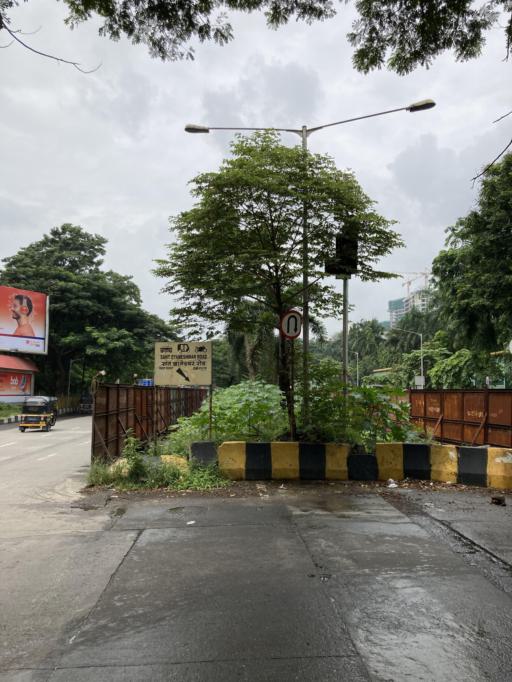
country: IN
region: Maharashtra
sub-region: Mumbai Suburban
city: Mumbai
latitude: 19.0582
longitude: 72.8537
